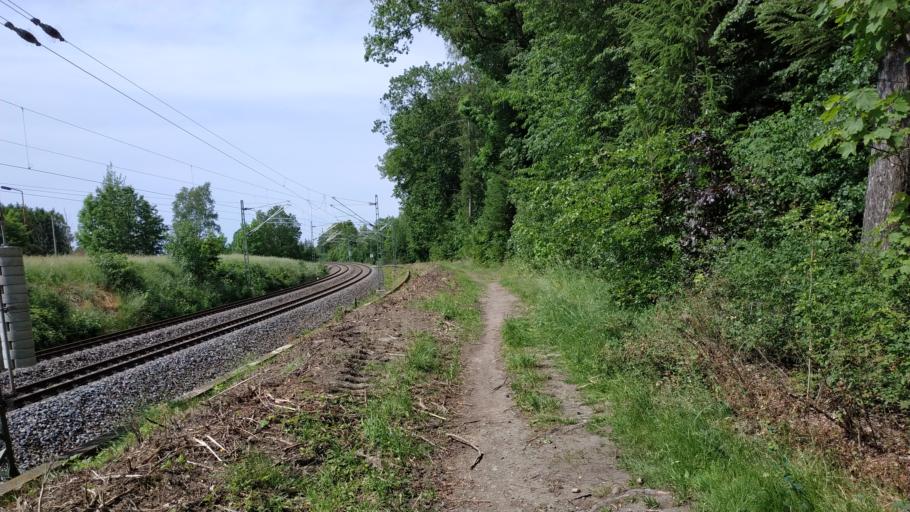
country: DE
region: Saxony
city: Plauen
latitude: 50.5313
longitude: 12.1189
